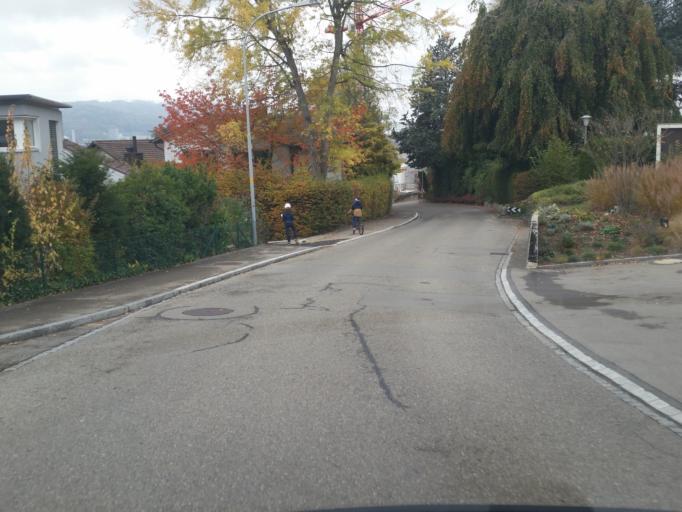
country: CH
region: Zurich
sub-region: Bezirk Dietikon
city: Geroldswil
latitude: 47.4219
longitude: 8.4144
